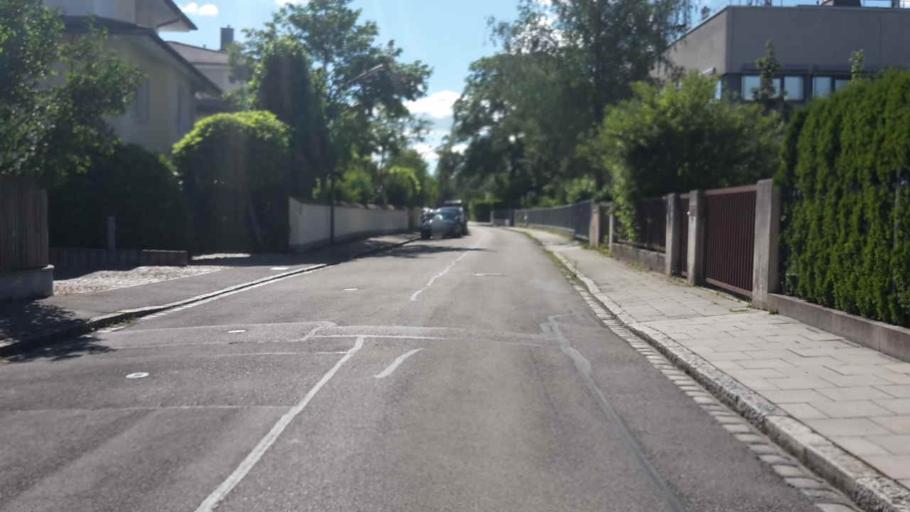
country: DE
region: Bavaria
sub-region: Upper Bavaria
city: Pasing
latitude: 48.1672
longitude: 11.4685
